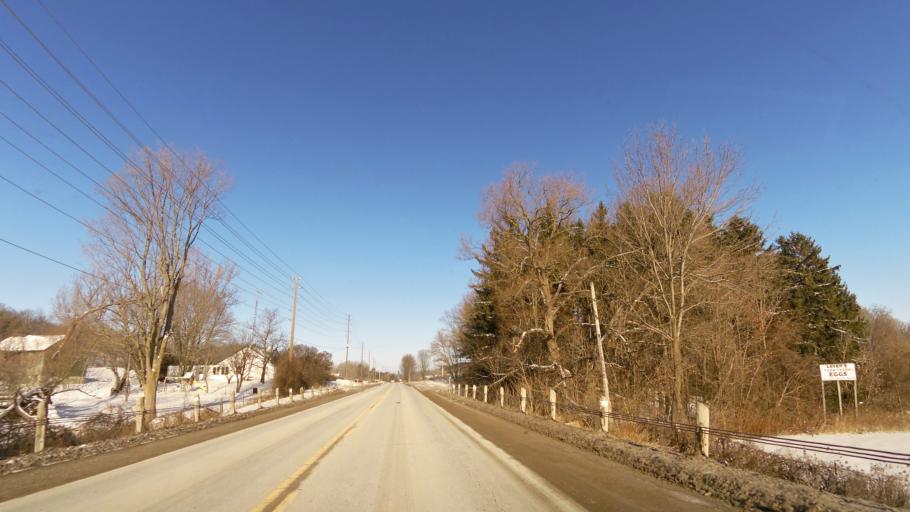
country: CA
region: Ontario
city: Quinte West
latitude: 44.1907
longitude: -77.8142
